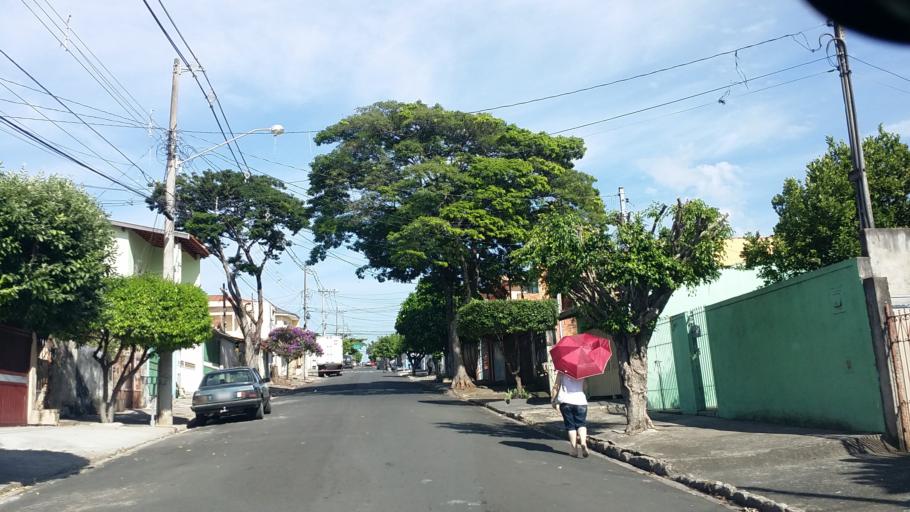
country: BR
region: Sao Paulo
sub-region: Indaiatuba
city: Indaiatuba
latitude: -23.1231
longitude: -47.2381
